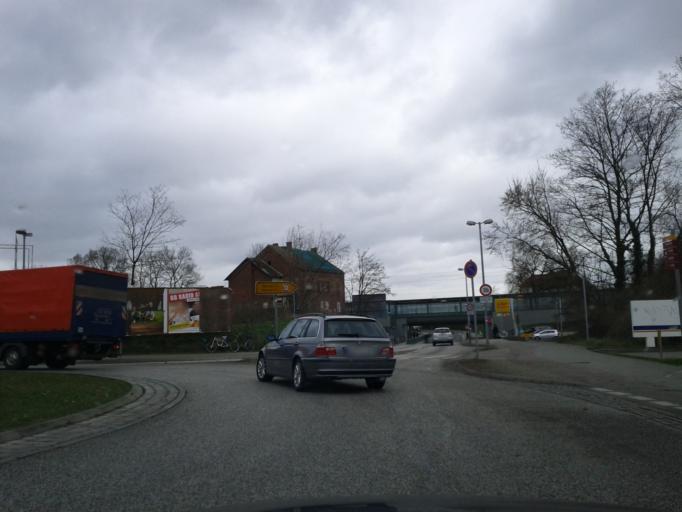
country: DE
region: Brandenburg
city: Erkner
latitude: 52.4266
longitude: 13.7508
